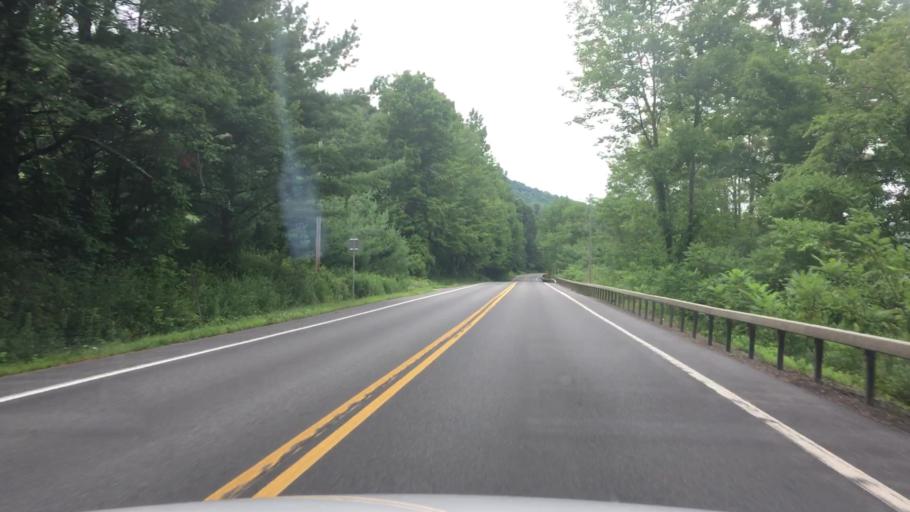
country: US
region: New York
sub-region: Otsego County
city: Otego
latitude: 42.4066
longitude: -75.1490
